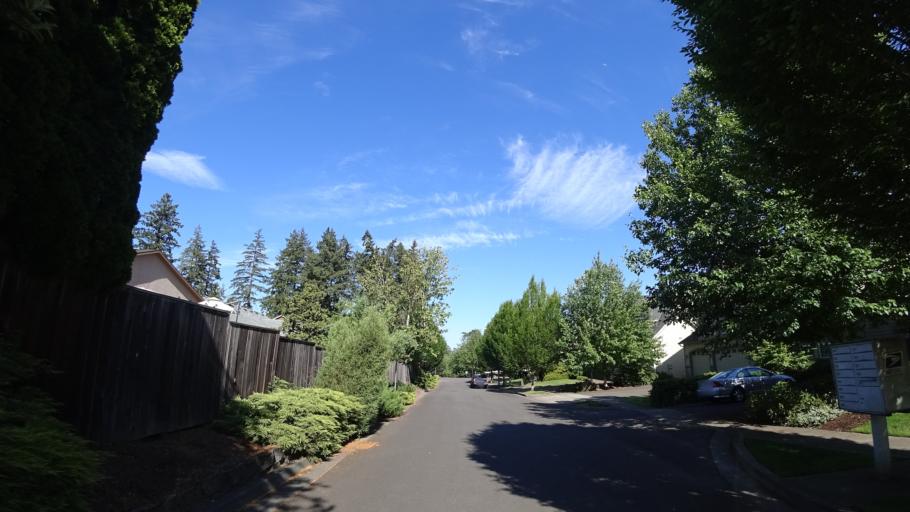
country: US
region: Oregon
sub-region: Washington County
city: Beaverton
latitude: 45.4534
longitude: -122.8116
